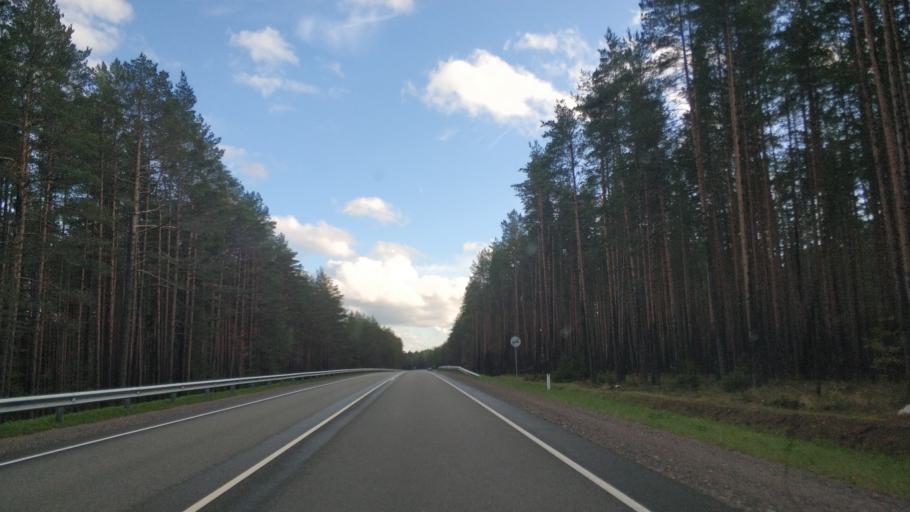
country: RU
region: Leningrad
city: Priozersk
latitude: 60.9907
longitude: 30.1833
